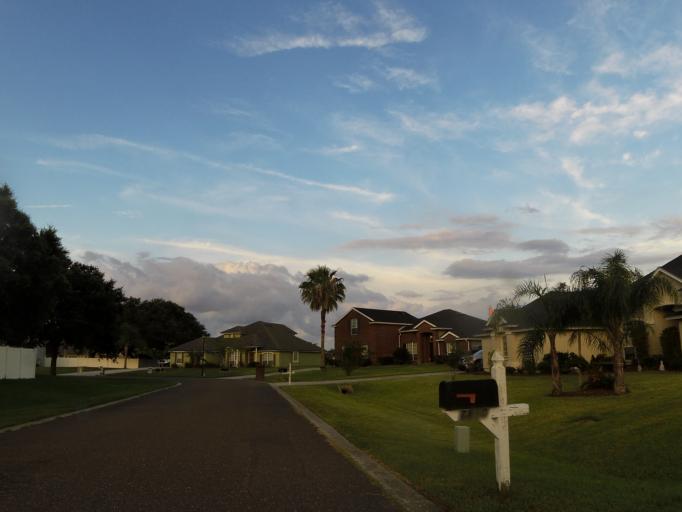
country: US
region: Florida
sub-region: Duval County
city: Atlantic Beach
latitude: 30.3957
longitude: -81.4961
